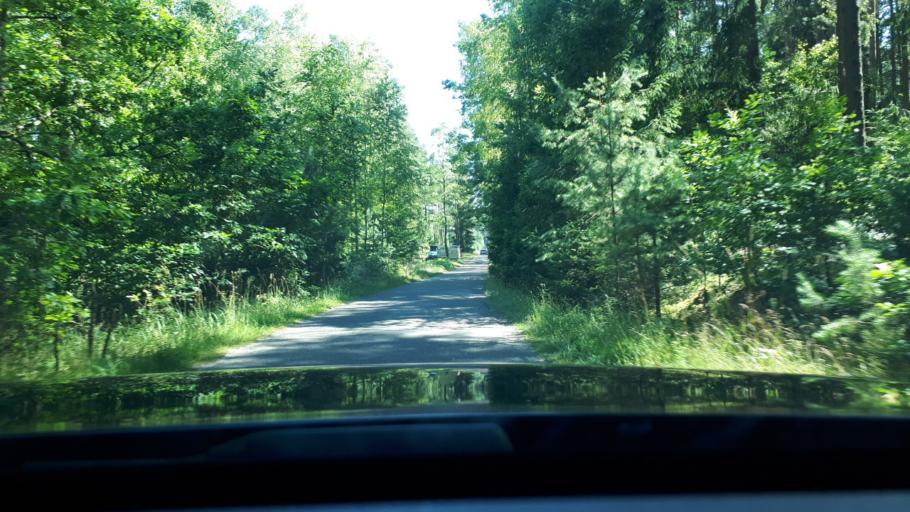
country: PL
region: Warmian-Masurian Voivodeship
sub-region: Powiat olsztynski
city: Stawiguda
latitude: 53.5766
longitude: 20.4550
